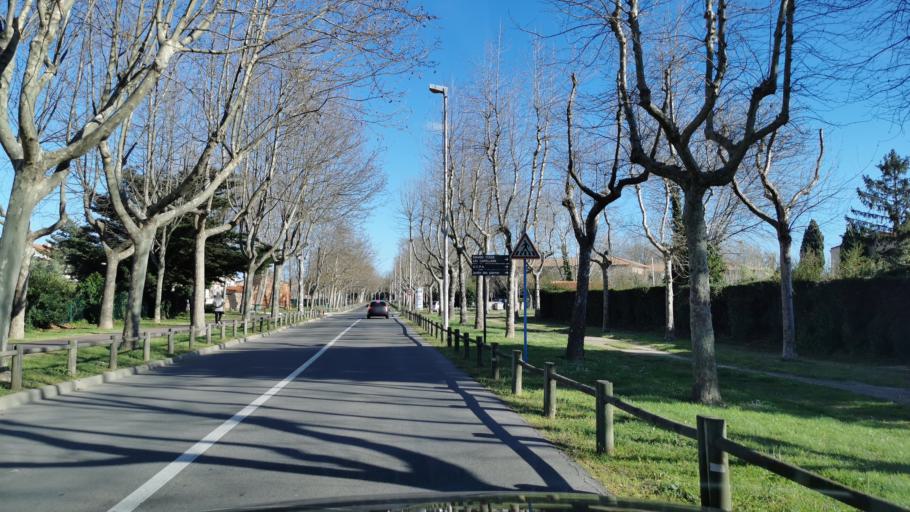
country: FR
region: Languedoc-Roussillon
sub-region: Departement des Pyrenees-Orientales
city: Saint-Cyprien-Plage
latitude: 42.6090
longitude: 3.0306
